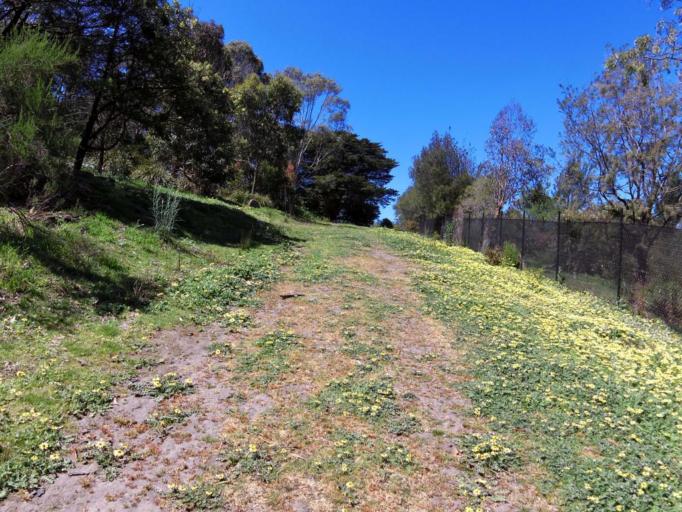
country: AU
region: Victoria
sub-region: Yarra Ranges
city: Lysterfield
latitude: -37.9556
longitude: 145.2824
